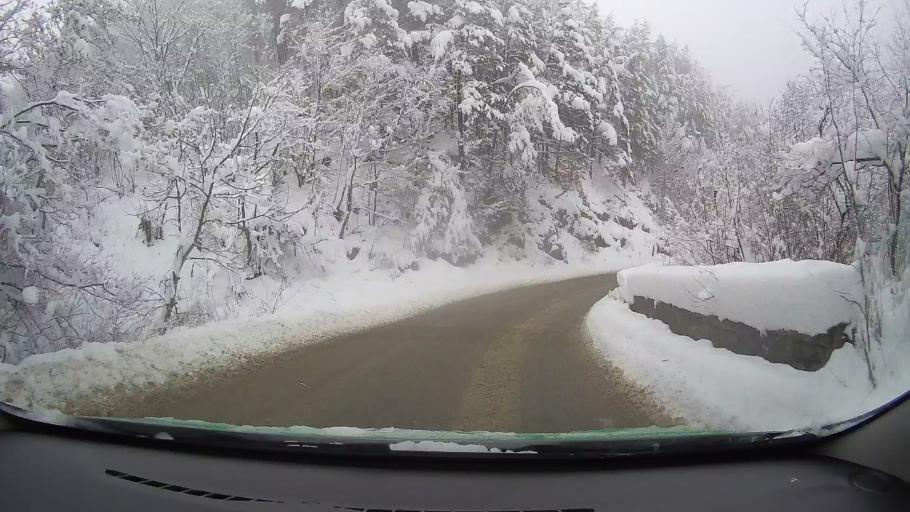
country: RO
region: Sibiu
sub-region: Comuna Tilisca
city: Tilisca
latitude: 45.8011
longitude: 23.7958
